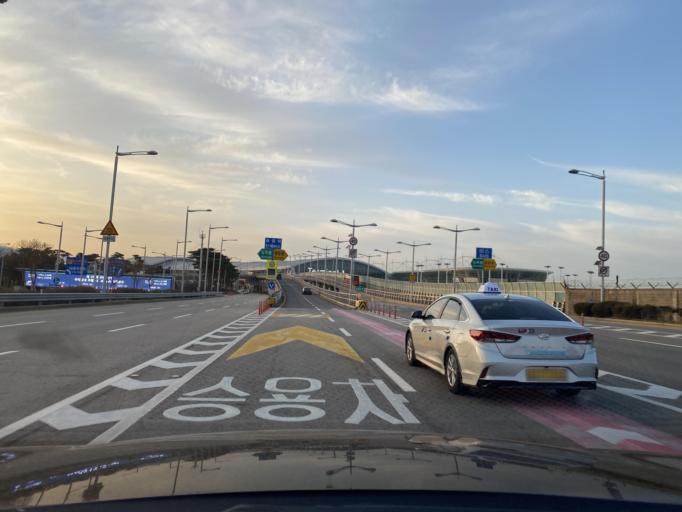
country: KR
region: Incheon
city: Incheon
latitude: 37.4479
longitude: 126.4590
